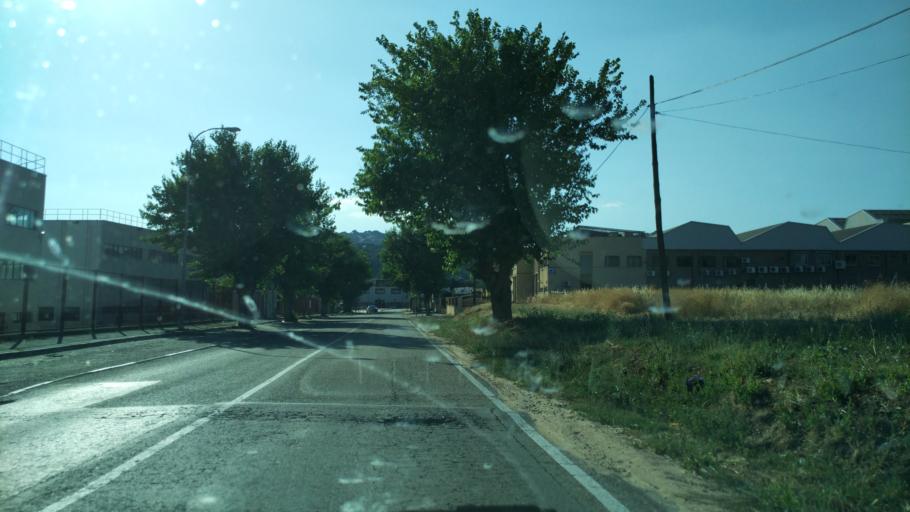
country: ES
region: Madrid
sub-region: Provincia de Madrid
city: San Agustin de Guadalix
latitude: 40.6907
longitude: -3.6064
